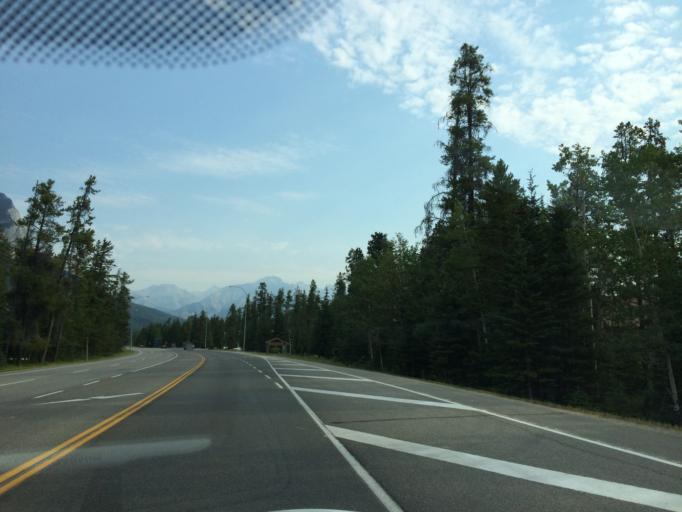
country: CA
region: Alberta
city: Banff
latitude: 51.1984
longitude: -115.5379
